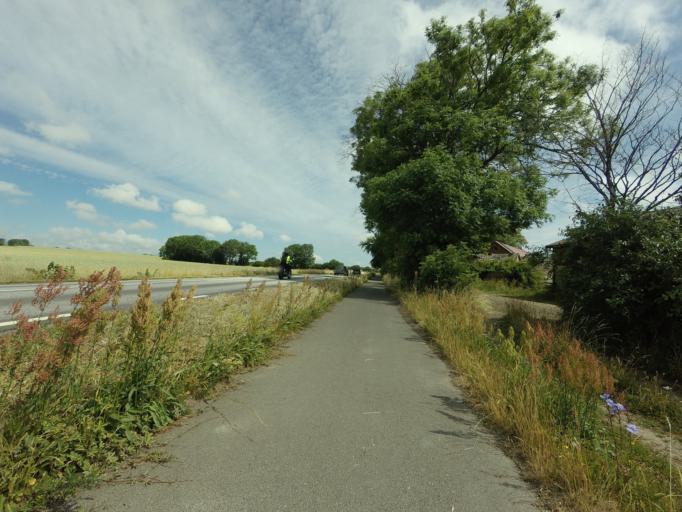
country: SE
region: Skane
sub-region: Simrishamns Kommun
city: Simrishamn
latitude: 55.5076
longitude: 14.3340
